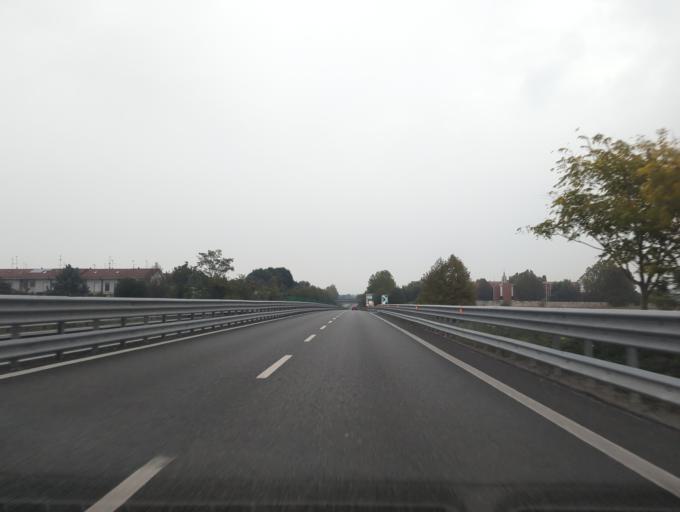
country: IT
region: Piedmont
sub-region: Provincia di Novara
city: Torrion Quartara
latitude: 45.4243
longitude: 8.6127
